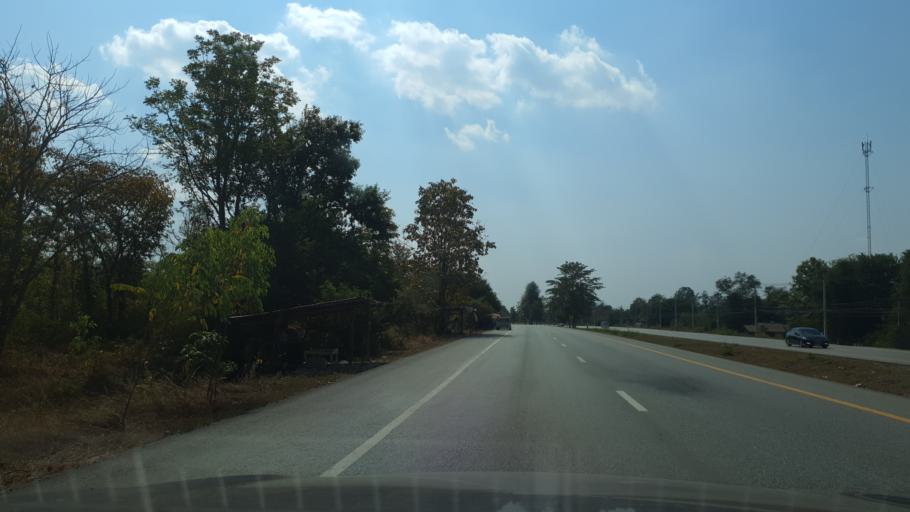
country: TH
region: Tak
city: Sam Ngao
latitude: 17.2977
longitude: 99.1443
